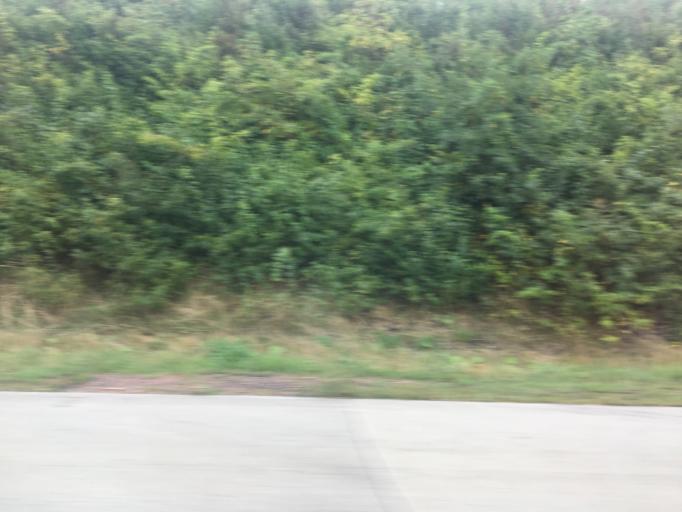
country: DE
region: Saxony
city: Stollberg
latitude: 50.7178
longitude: 12.7648
